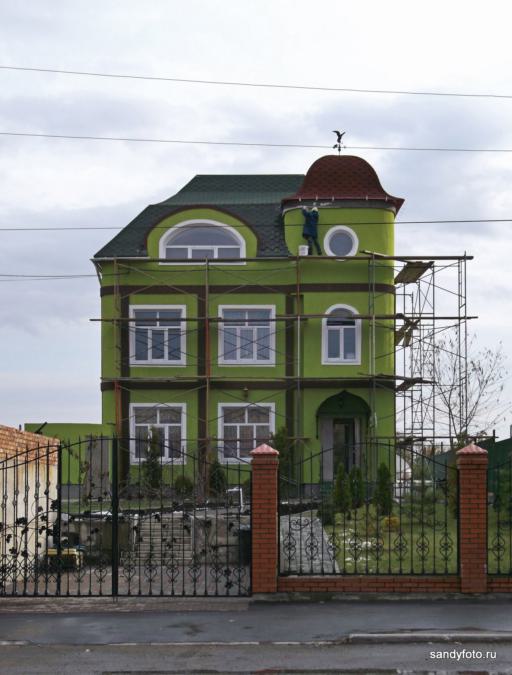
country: RU
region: Chelyabinsk
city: Troitsk
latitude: 54.0774
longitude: 61.5402
